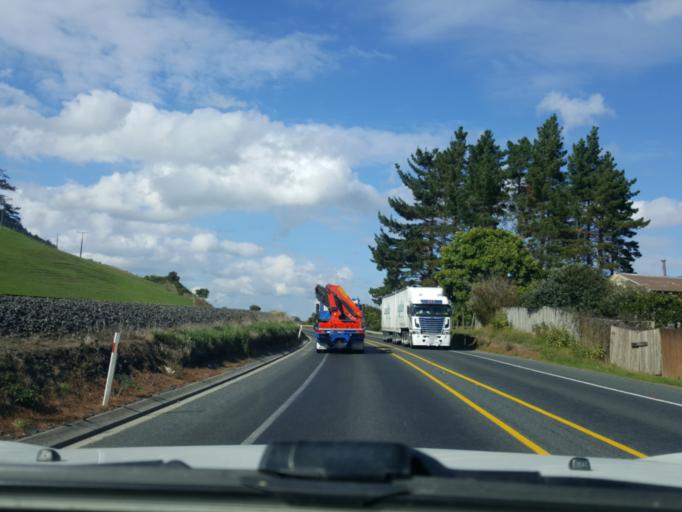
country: NZ
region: Waikato
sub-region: Waikato District
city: Ngaruawahia
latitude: -37.5991
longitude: 175.1642
